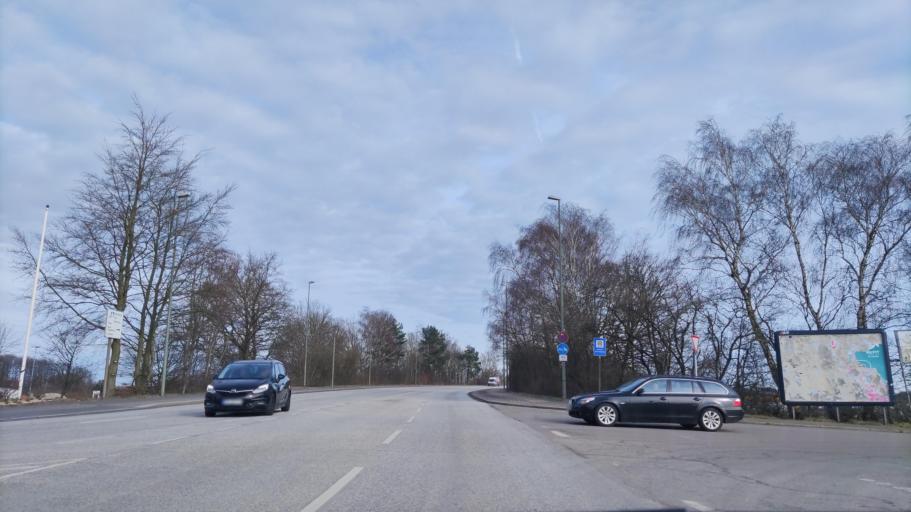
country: DE
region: Schleswig-Holstein
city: Neumunster
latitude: 54.0892
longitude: 9.9777
